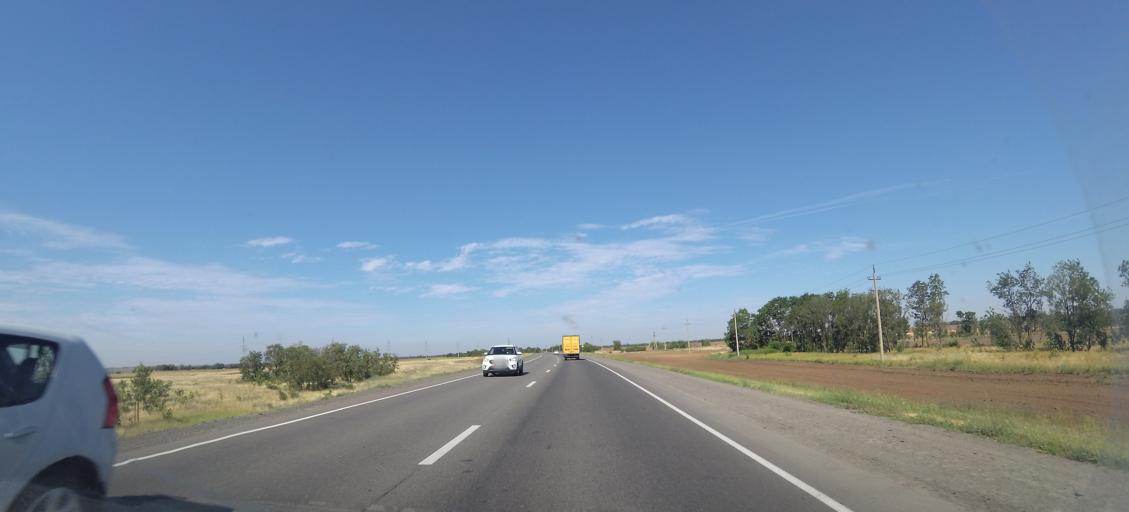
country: RU
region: Volgograd
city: Oktyabr'skiy
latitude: 48.6989
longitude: 43.8131
